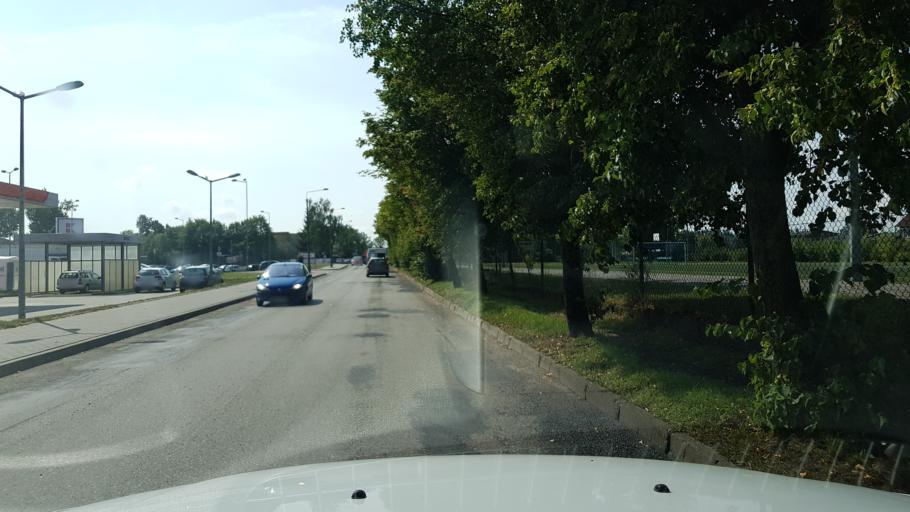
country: PL
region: West Pomeranian Voivodeship
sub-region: Powiat walecki
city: Walcz
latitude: 53.2765
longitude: 16.4857
